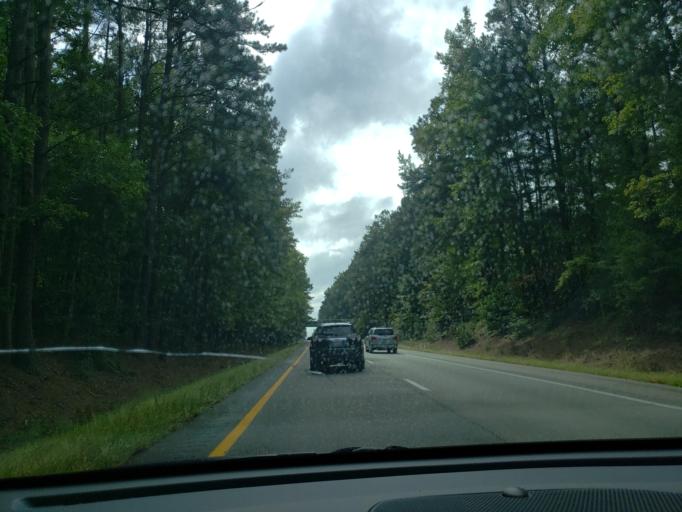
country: US
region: Virginia
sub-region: Brunswick County
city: Lawrenceville
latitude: 36.8962
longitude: -77.8009
